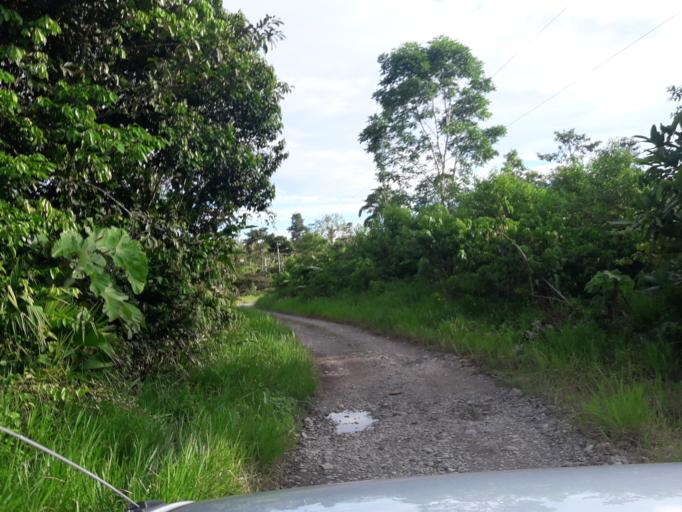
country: EC
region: Orellana
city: Boca Suno
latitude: -0.9020
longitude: -77.3113
